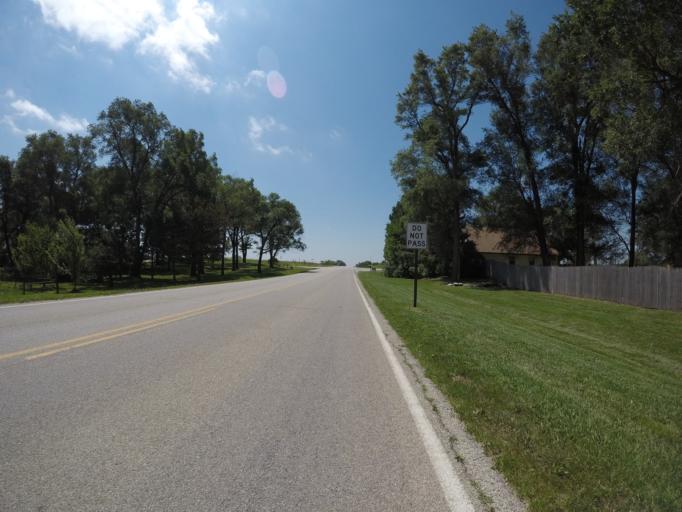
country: US
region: Kansas
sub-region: Pottawatomie County
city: Westmoreland
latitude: 39.3202
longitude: -96.4361
